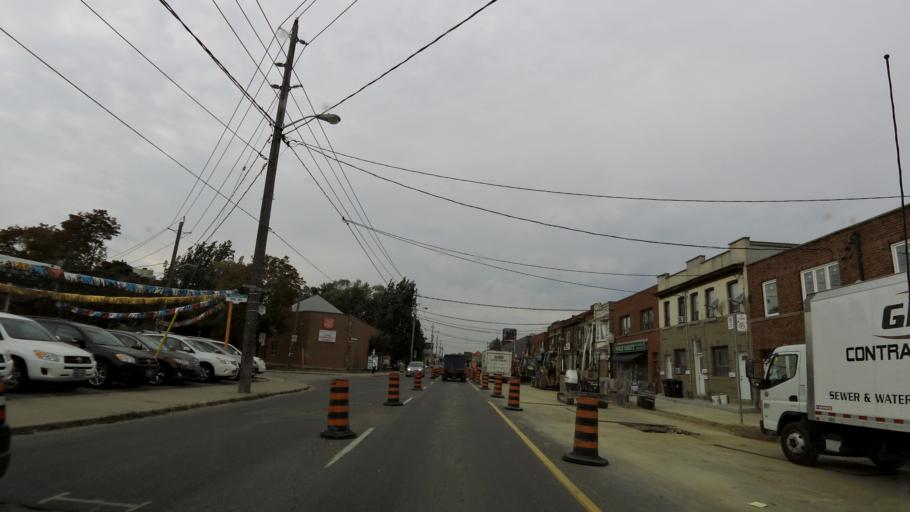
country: CA
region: Ontario
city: Toronto
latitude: 43.6856
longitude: -79.4869
